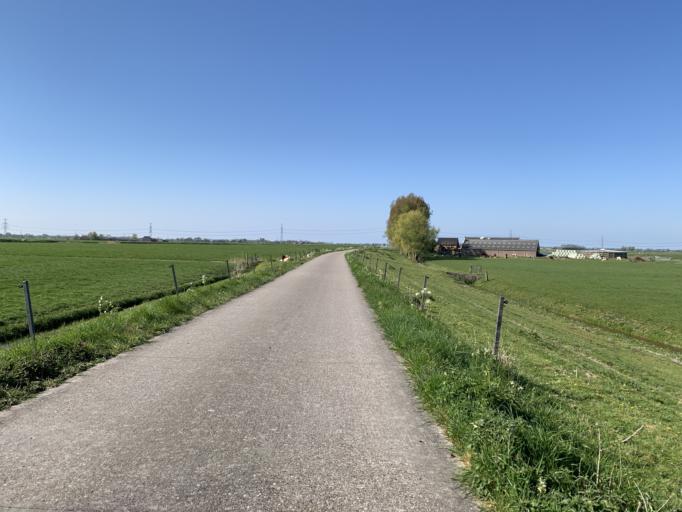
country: NL
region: Groningen
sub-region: Gemeente Zuidhorn
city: Aduard
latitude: 53.2791
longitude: 6.5054
